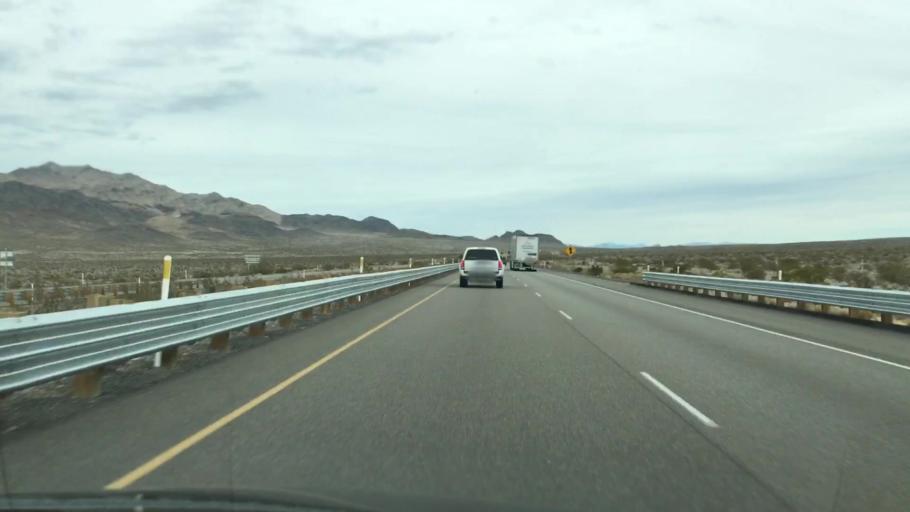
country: US
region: Nevada
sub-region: Nye County
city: Pahrump
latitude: 36.5986
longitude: -115.9944
